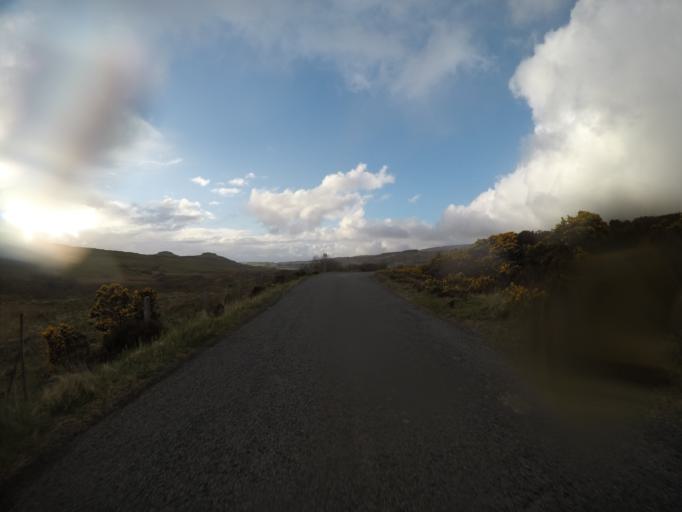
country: GB
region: Scotland
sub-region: Highland
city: Portree
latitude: 57.4697
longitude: -6.2997
